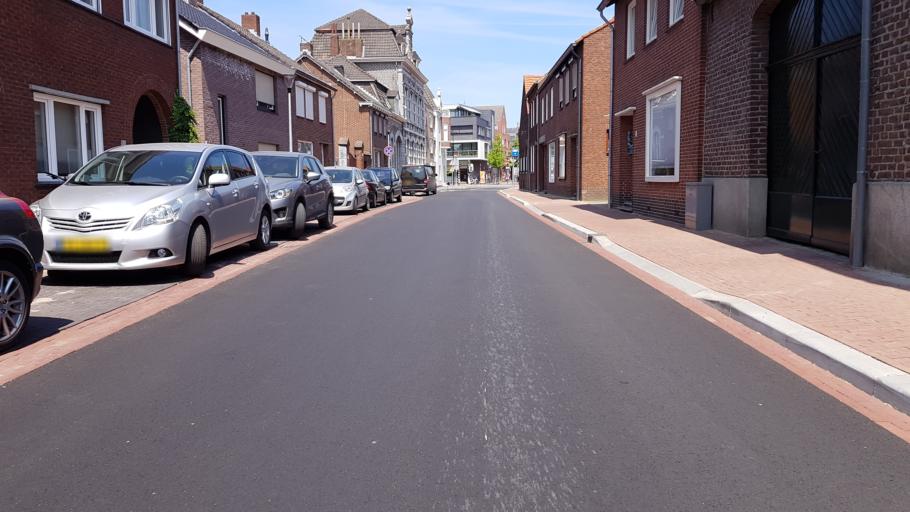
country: NL
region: Limburg
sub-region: Gemeente Maasgouw
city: Maasbracht
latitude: 51.1021
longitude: 5.8653
